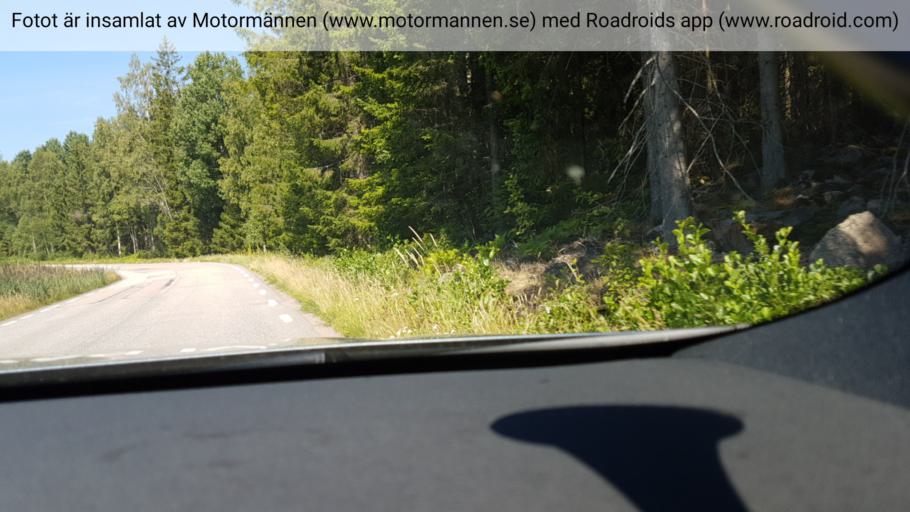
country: SE
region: Vaestra Goetaland
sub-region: Toreboda Kommun
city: Toereboda
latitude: 58.8243
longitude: 14.0082
